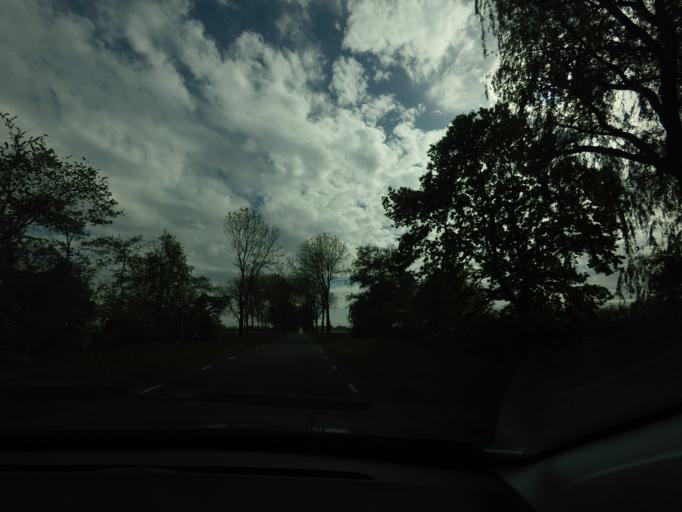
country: NL
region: North Holland
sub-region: Gemeente Beemster
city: Halfweg
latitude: 52.5320
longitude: 4.9029
